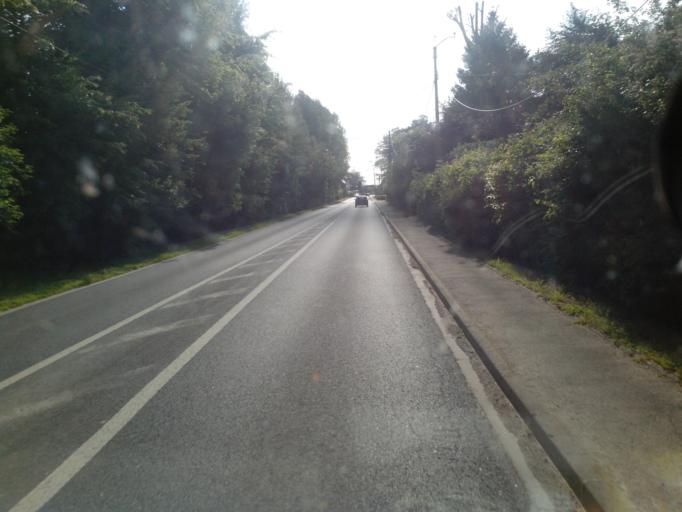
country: FR
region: Haute-Normandie
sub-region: Departement de la Seine-Maritime
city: Bosc-le-Hard
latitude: 49.6743
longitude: 1.1266
